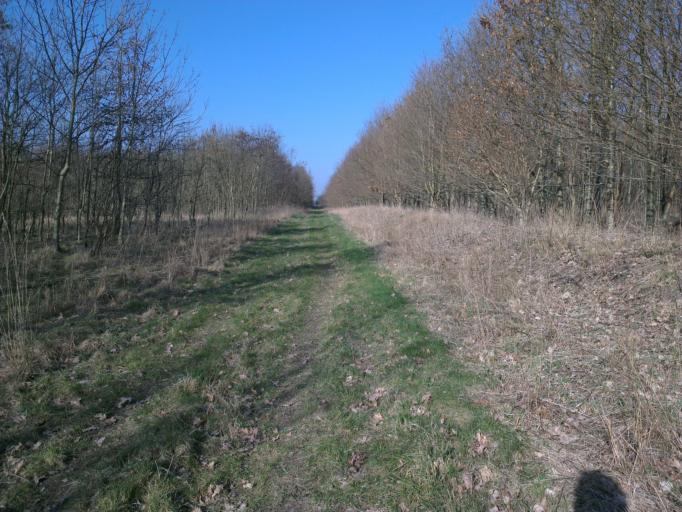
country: DK
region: Capital Region
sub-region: Frederikssund Kommune
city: Frederikssund
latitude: 55.8392
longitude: 12.0929
